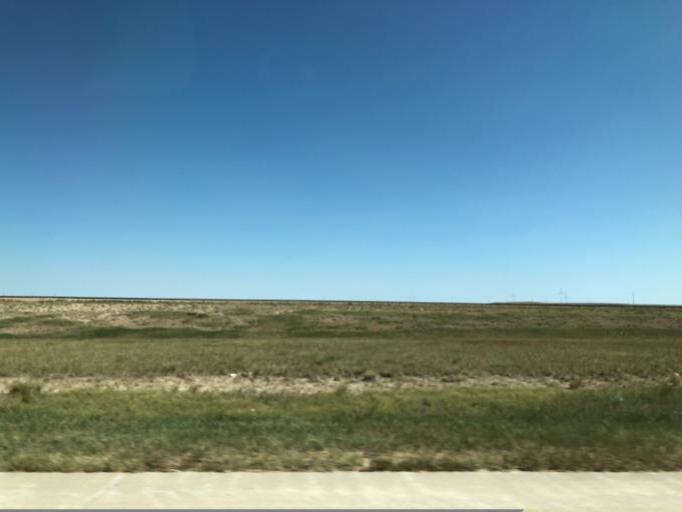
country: US
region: Colorado
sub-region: Lincoln County
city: Limon
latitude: 39.2680
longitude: -103.6230
